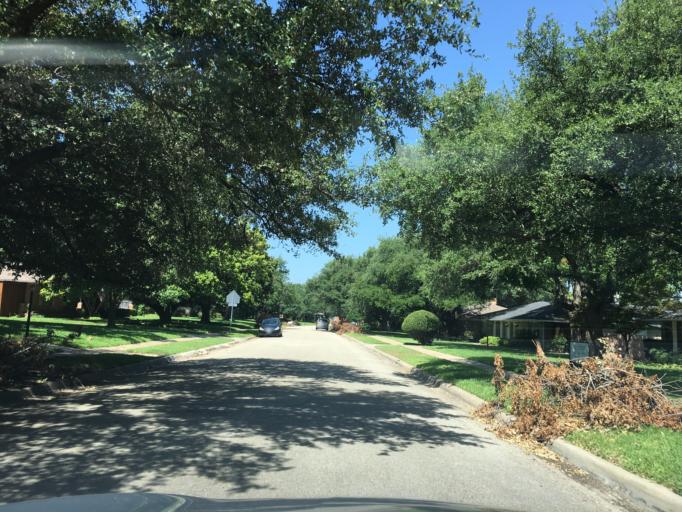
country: US
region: Texas
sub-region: Dallas County
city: University Park
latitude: 32.9039
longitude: -96.7856
